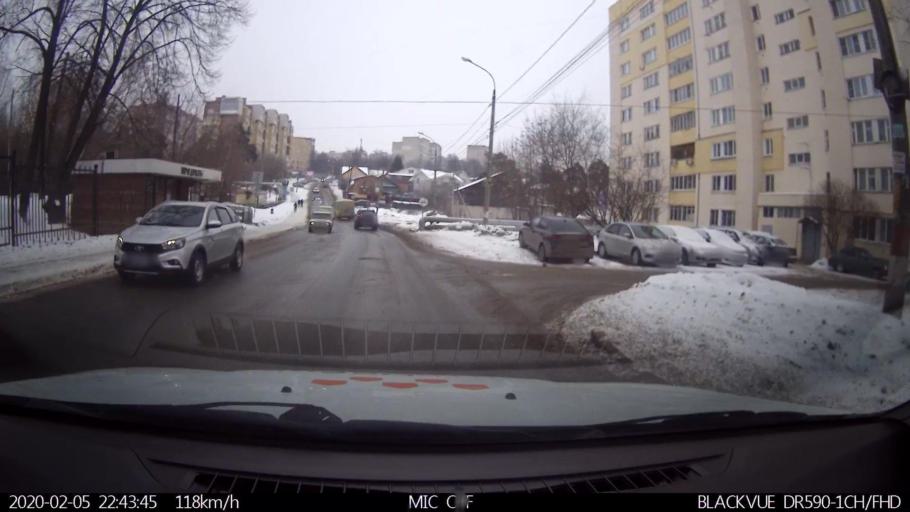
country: RU
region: Nizjnij Novgorod
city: Imeni Stepana Razina
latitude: 54.7117
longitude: 44.3861
